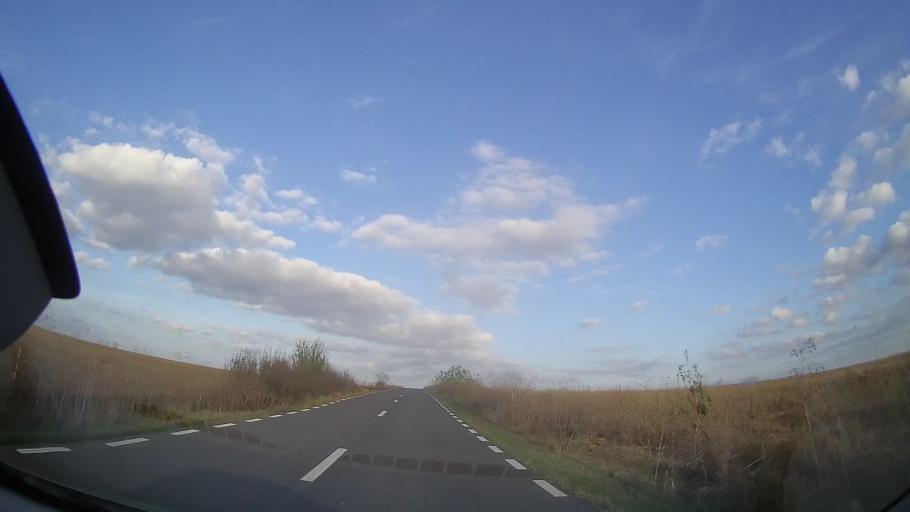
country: RO
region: Constanta
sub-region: Comuna Independenta
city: Independenta
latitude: 43.9381
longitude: 28.0393
